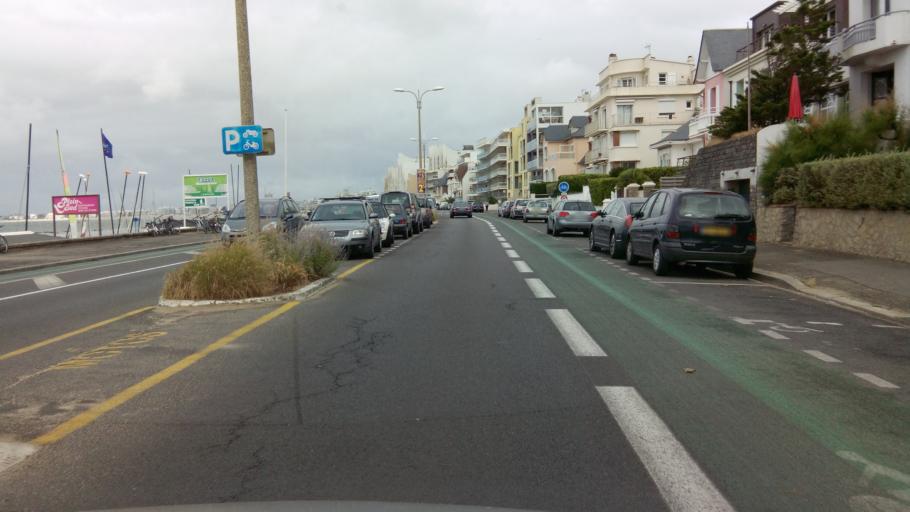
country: FR
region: Pays de la Loire
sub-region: Departement de la Loire-Atlantique
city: Pornichet
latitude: 47.2710
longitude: -2.3530
